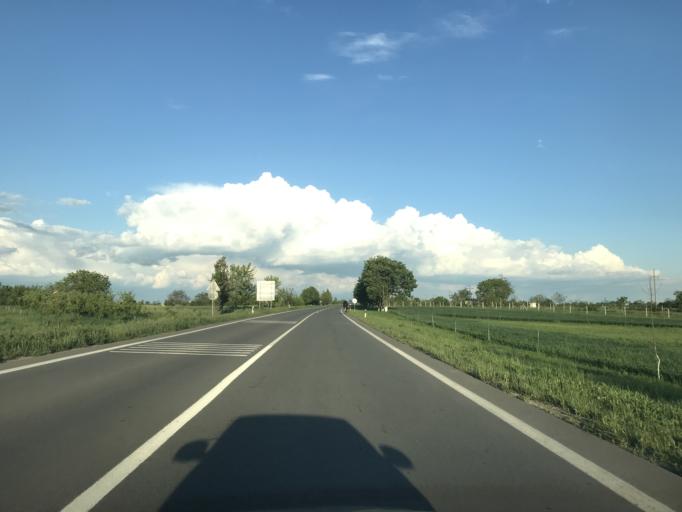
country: RS
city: Aradac
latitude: 45.3915
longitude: 20.2998
